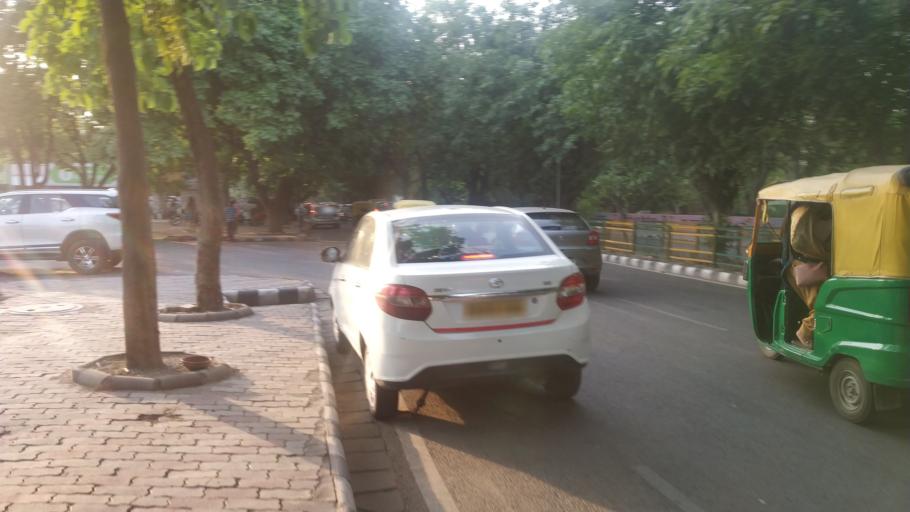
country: IN
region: Punjab
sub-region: Ajitgarh
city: Mohali
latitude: 30.7090
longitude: 76.7231
